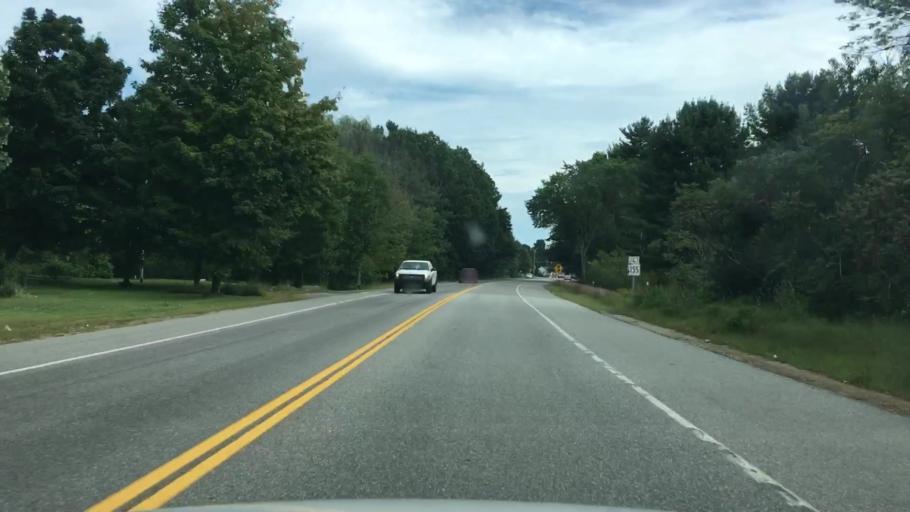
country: US
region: New Hampshire
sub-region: Strafford County
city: Dover
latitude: 43.1854
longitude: -70.8945
